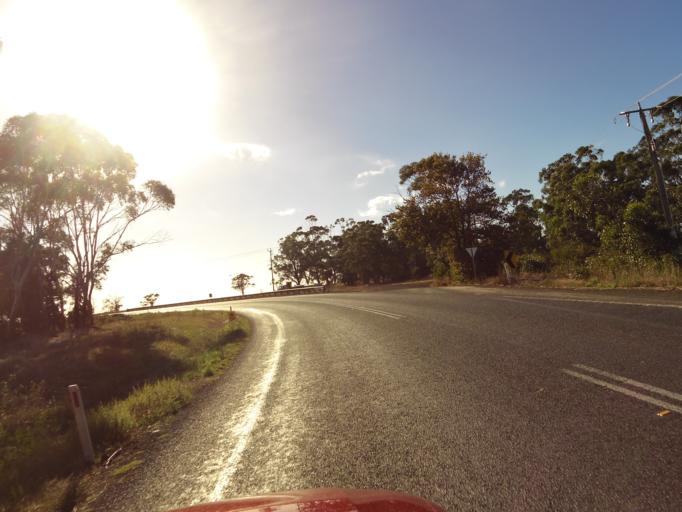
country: AU
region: Victoria
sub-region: Warrnambool
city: Allansford
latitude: -38.4032
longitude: 143.0012
